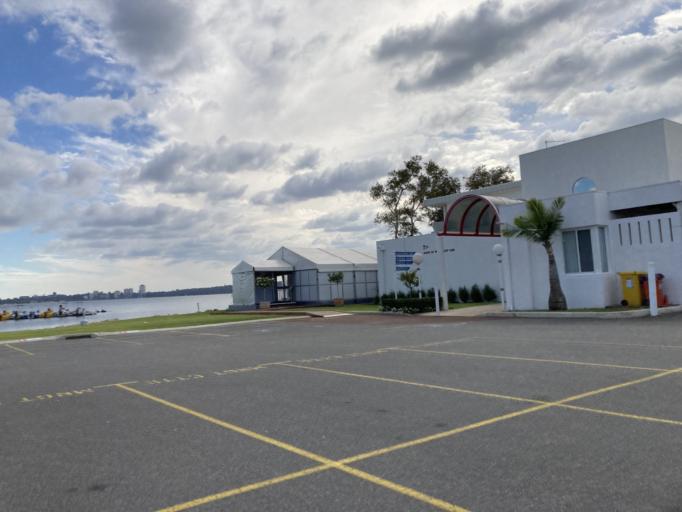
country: AU
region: Western Australia
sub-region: Melville
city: Applecross
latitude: -32.0025
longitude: 115.8458
